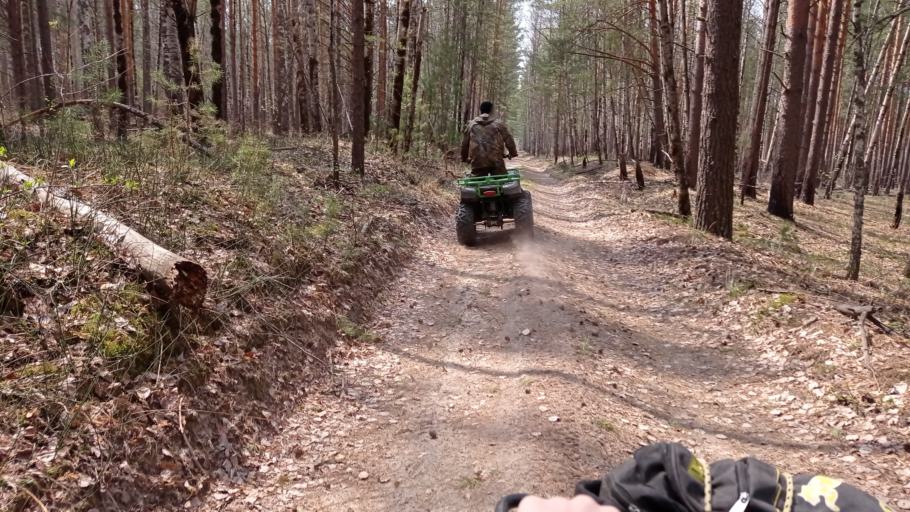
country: RU
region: Tomsk
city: Timiryazevskoye
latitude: 56.4363
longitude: 84.6529
